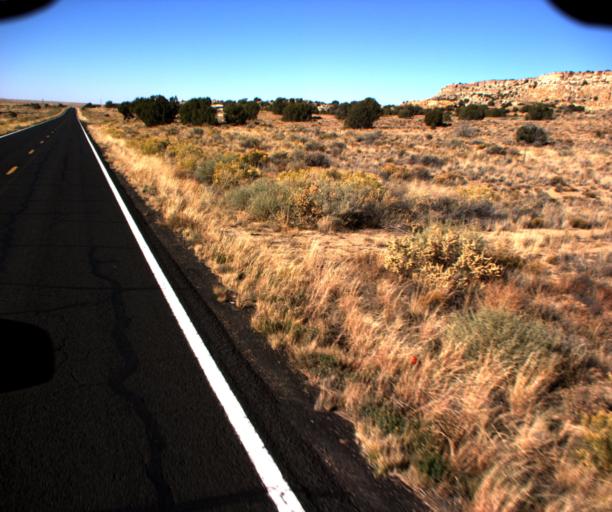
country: US
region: Arizona
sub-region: Navajo County
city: First Mesa
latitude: 35.8367
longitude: -110.2624
